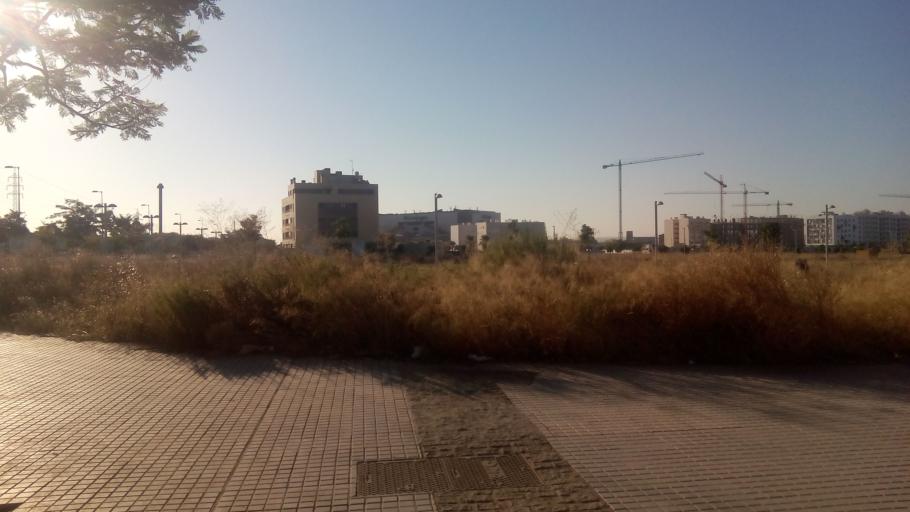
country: ES
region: Andalusia
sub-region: Province of Cordoba
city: Cordoba
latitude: 37.8964
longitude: -4.8145
